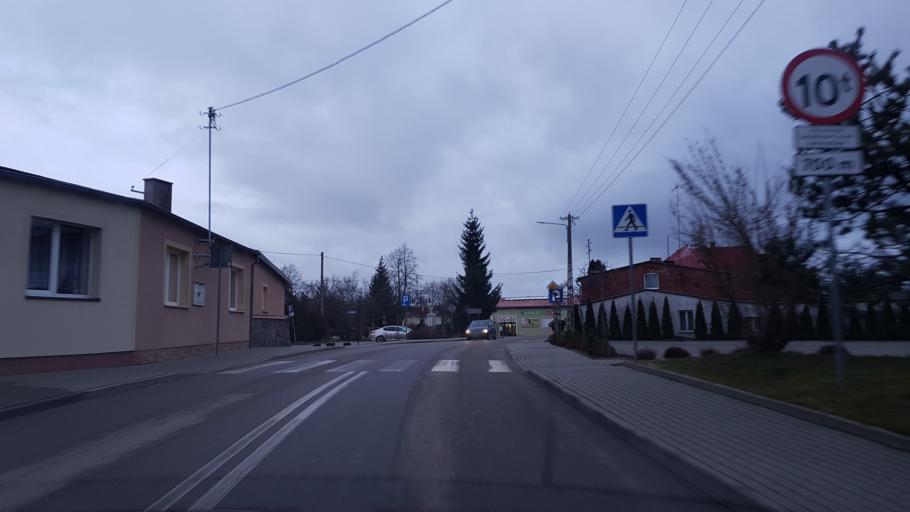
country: PL
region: Pomeranian Voivodeship
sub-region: Powiat bytowski
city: Tuchomie
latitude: 54.1153
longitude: 17.3367
